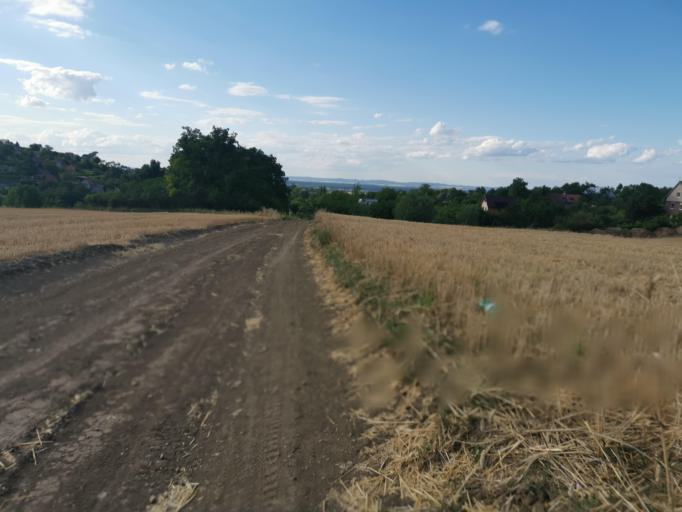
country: SK
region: Trnavsky
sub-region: Okres Skalica
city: Skalica
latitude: 48.8295
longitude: 17.2530
